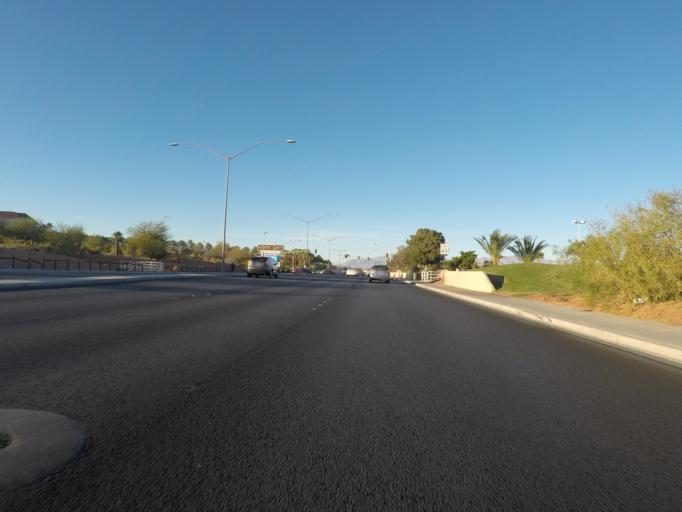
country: US
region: Nevada
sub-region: Clark County
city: Summerlin South
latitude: 36.1728
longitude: -115.2870
